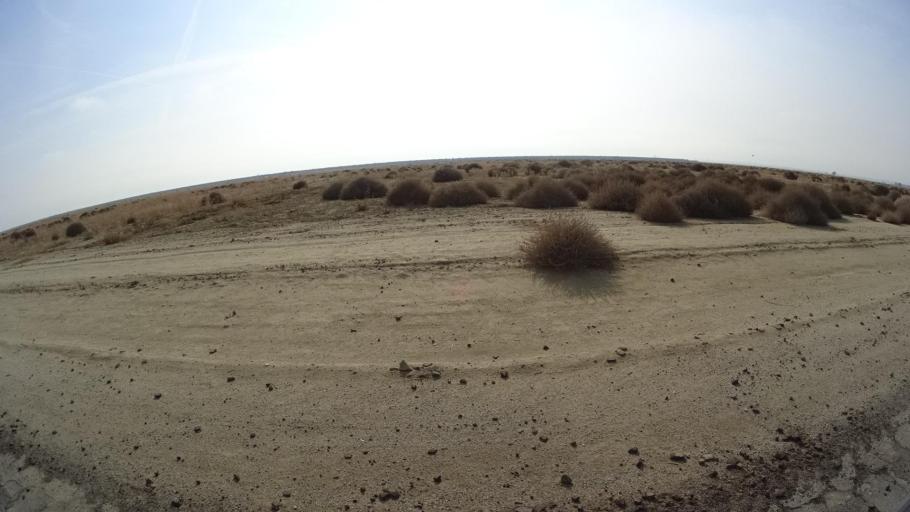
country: US
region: California
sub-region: Kern County
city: Arvin
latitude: 35.0309
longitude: -118.8941
